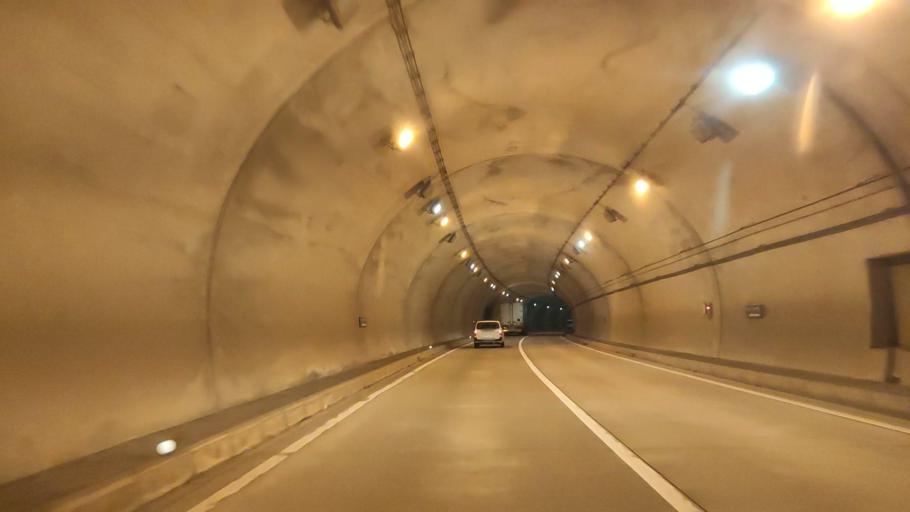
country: JP
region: Toyama
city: Yatsuomachi-higashikumisaka
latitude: 36.5282
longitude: 137.2274
